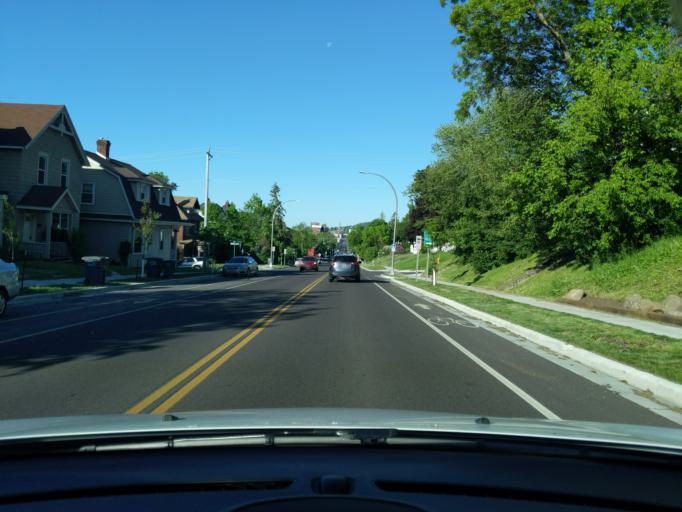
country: US
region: Minnesota
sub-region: Saint Louis County
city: Duluth
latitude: 46.8044
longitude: -92.0834
